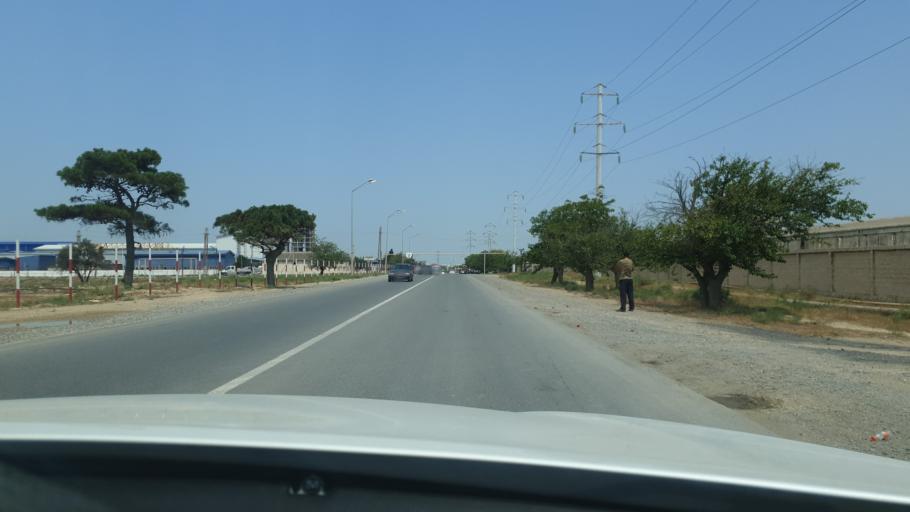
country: AZ
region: Baki
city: Qaracuxur
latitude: 40.3971
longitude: 49.9992
